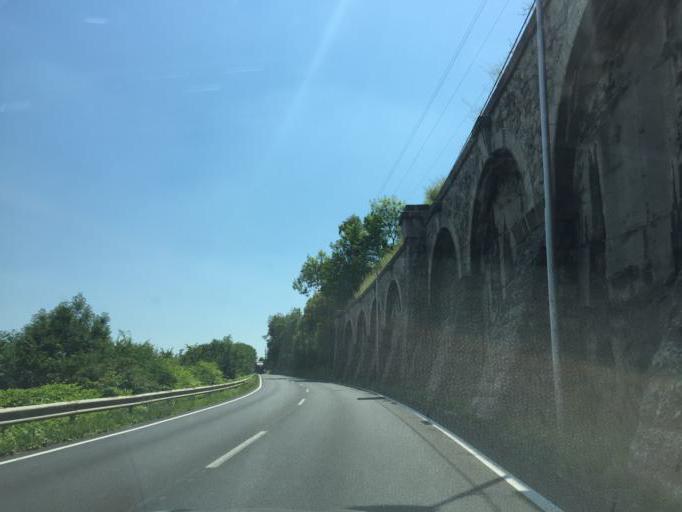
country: SI
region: Kranj
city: Kranj
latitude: 46.2346
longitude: 14.3491
